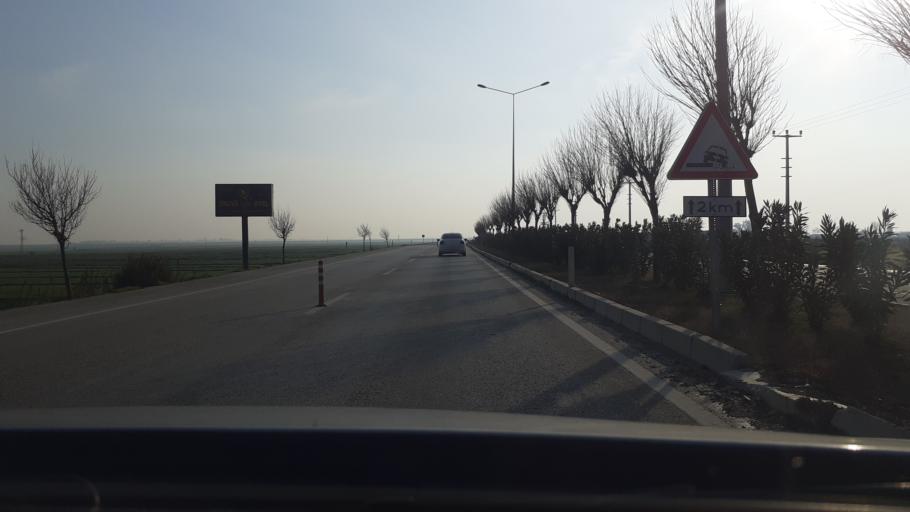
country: TR
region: Hatay
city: Serinyol
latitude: 36.3711
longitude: 36.2477
